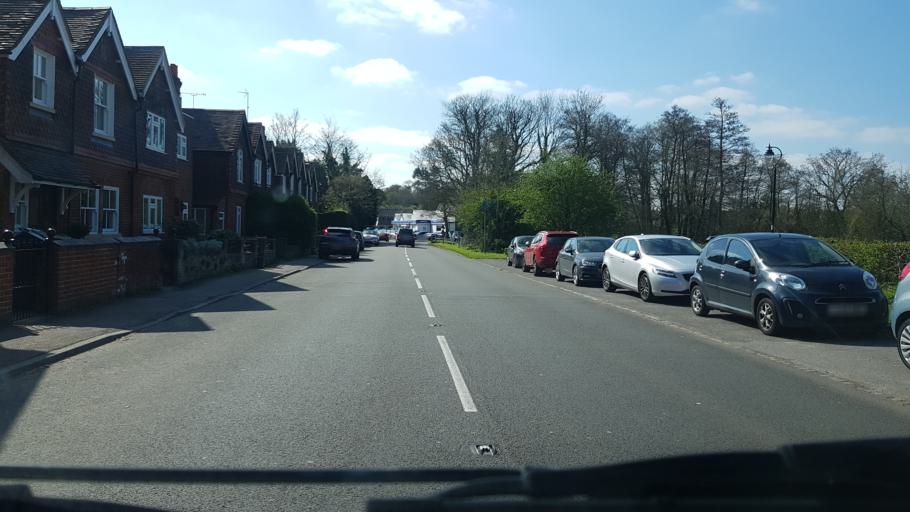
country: GB
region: England
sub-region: Surrey
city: Pirbright
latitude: 51.2931
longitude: -0.6458
